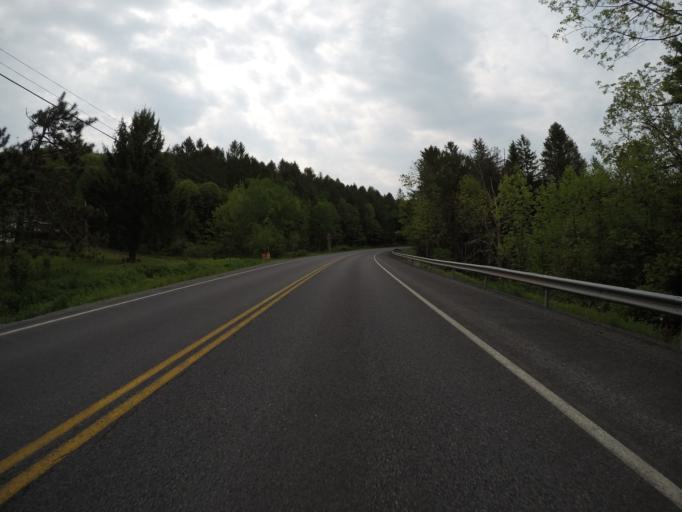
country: US
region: New York
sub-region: Sullivan County
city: Livingston Manor
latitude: 42.0432
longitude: -74.9048
